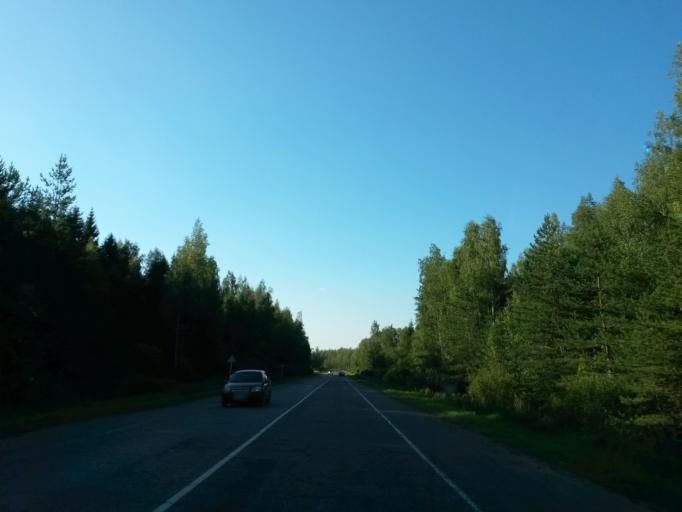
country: RU
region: Ivanovo
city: Pistsovo
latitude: 57.0831
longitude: 40.6728
